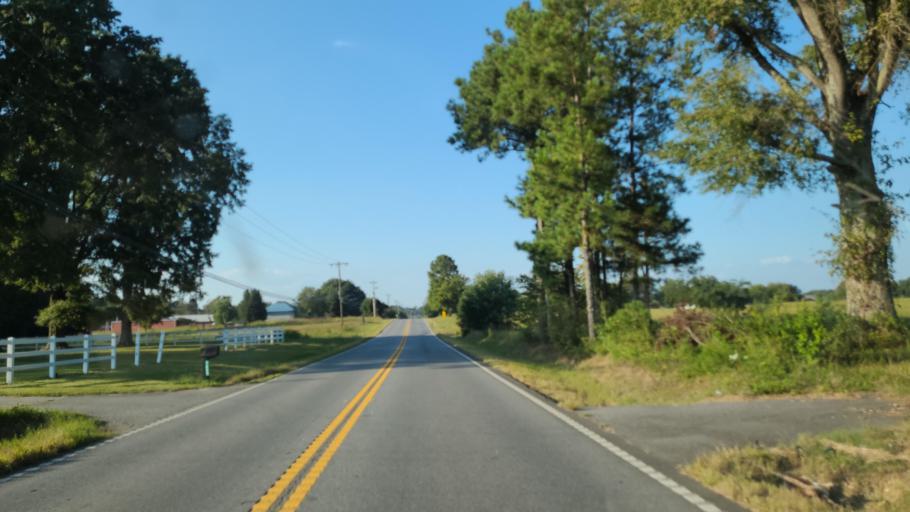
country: US
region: Georgia
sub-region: Murray County
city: Chatsworth
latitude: 34.8669
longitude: -84.7997
